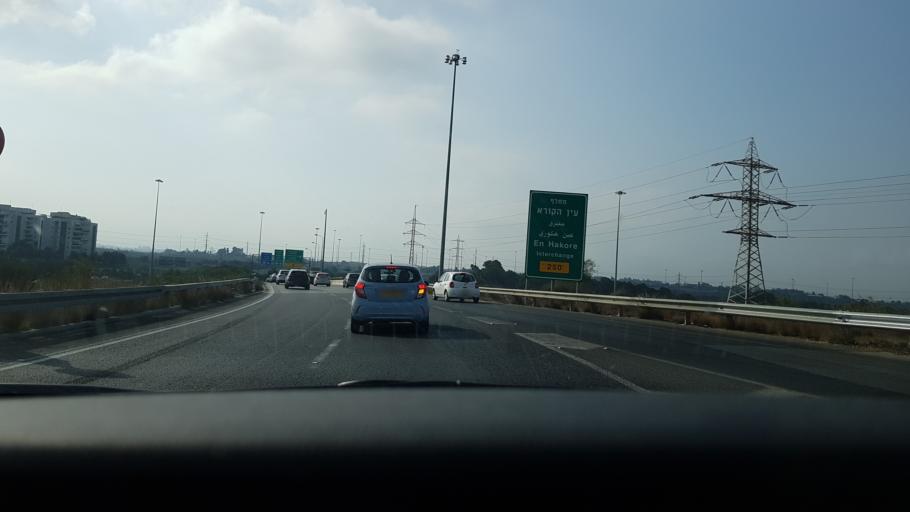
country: IL
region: Central District
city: Rishon LeZiyyon
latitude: 31.9631
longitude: 34.7846
